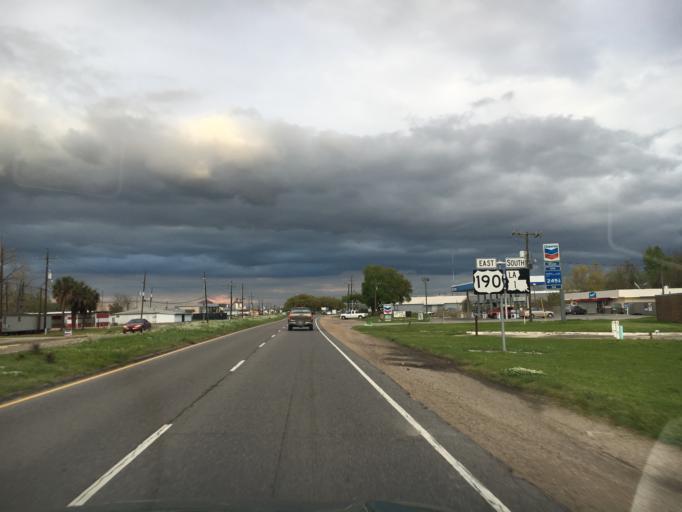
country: US
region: Louisiana
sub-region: West Baton Rouge Parish
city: Port Allen
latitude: 30.5055
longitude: -91.2233
